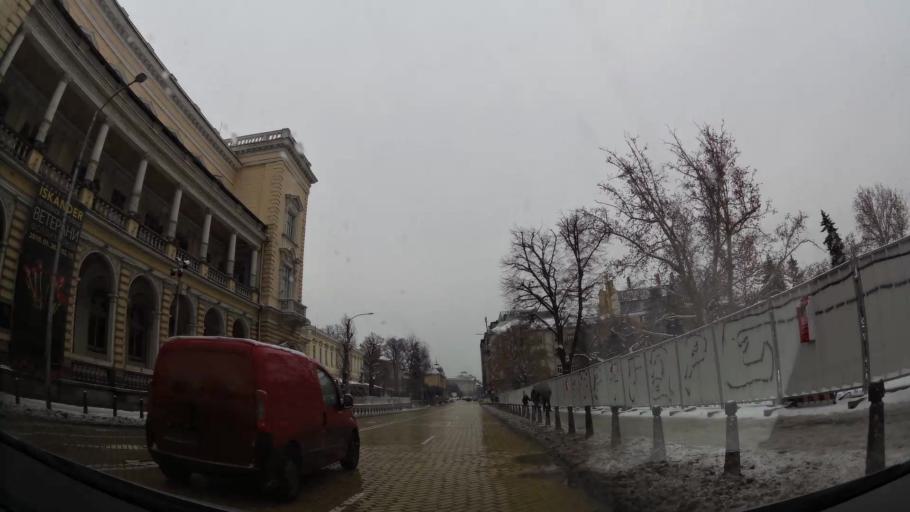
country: BG
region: Sofia-Capital
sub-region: Stolichna Obshtina
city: Sofia
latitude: 42.6951
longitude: 23.3295
